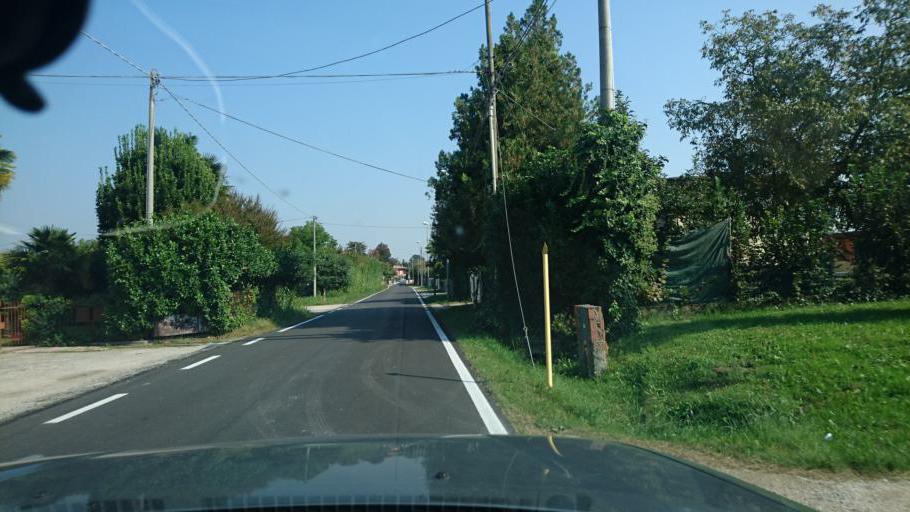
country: IT
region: Veneto
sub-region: Provincia di Padova
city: Ronchi di Campanile
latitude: 45.4489
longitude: 11.7738
